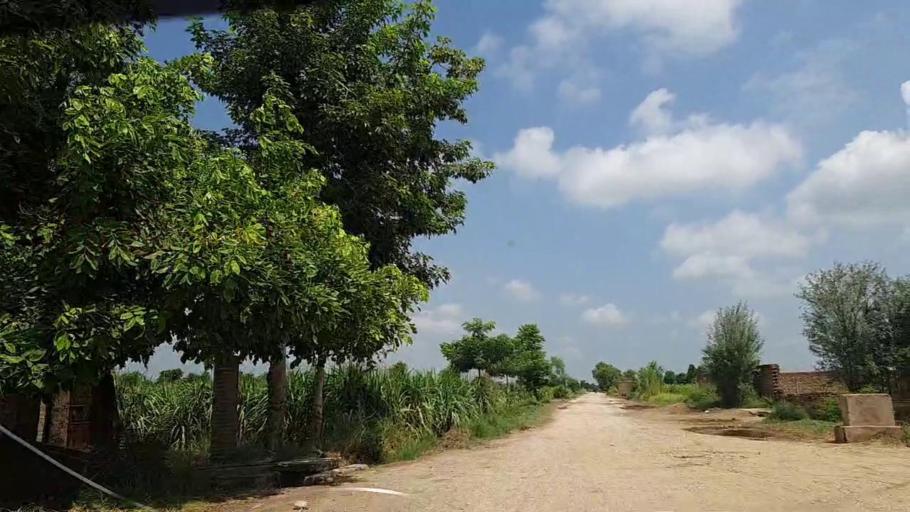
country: PK
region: Sindh
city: Tharu Shah
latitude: 26.8999
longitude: 68.0395
